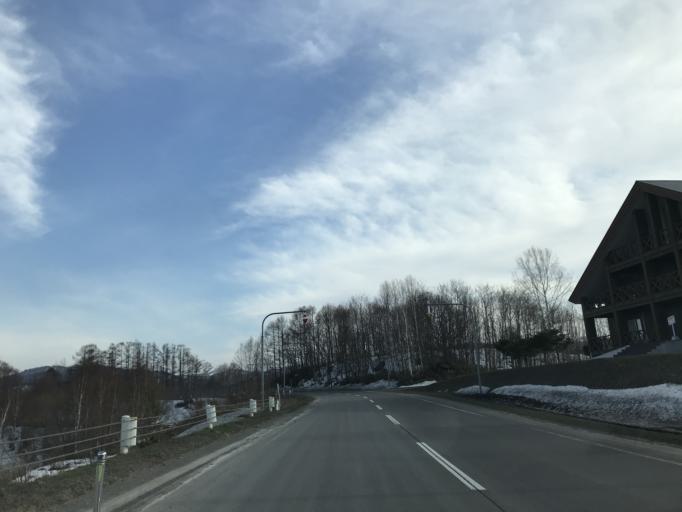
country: JP
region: Hokkaido
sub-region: Asahikawa-shi
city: Asahikawa
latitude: 43.7093
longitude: 142.3239
